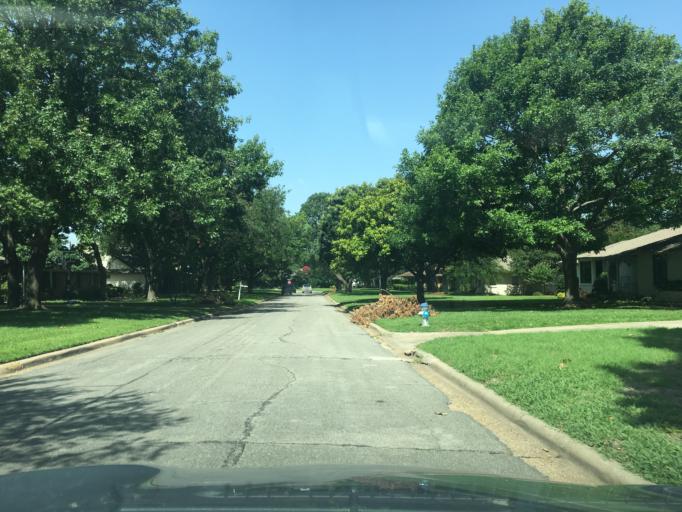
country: US
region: Texas
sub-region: Dallas County
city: University Park
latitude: 32.8995
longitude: -96.8053
